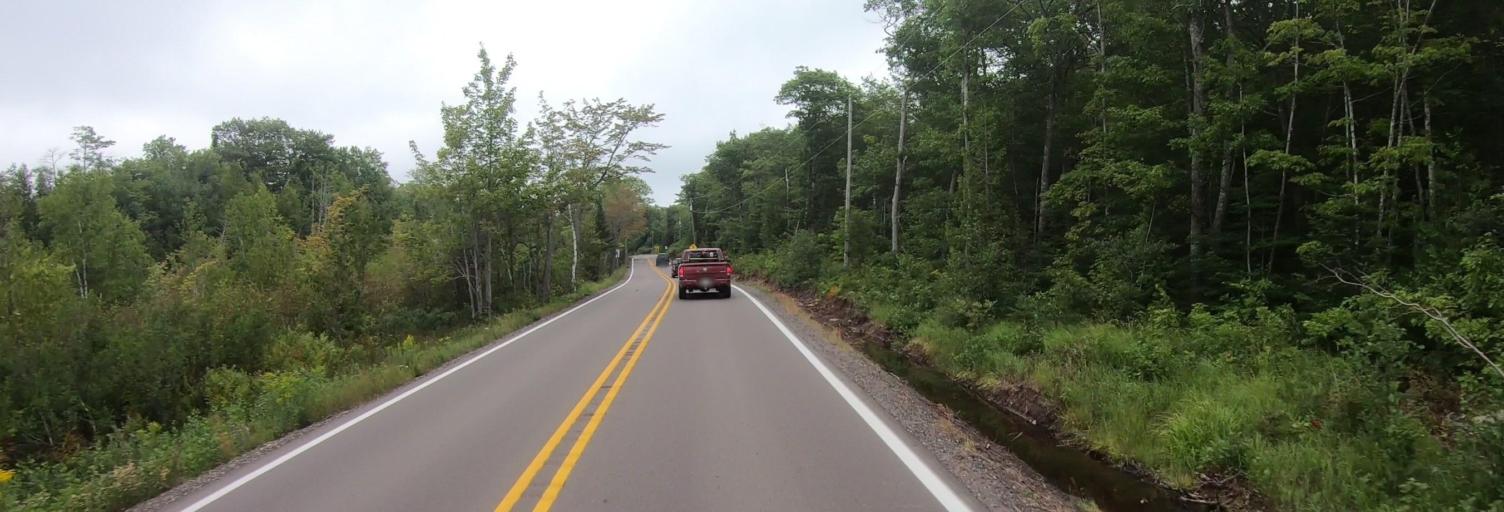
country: US
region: Michigan
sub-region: Keweenaw County
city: Eagle River
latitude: 47.4360
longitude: -87.9650
